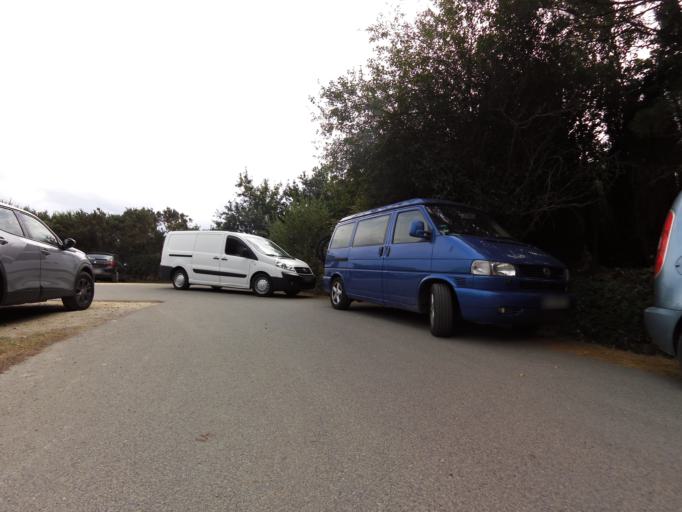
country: FR
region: Brittany
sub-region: Departement du Finistere
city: Beuzec-Cap-Sizun
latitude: 48.0943
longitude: -4.4680
